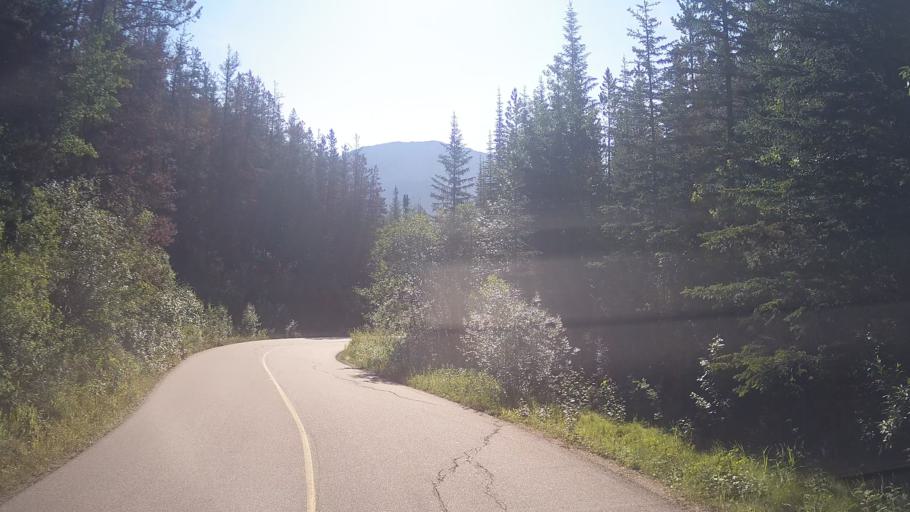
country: CA
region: Alberta
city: Jasper Park Lodge
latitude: 53.1774
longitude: -117.8591
